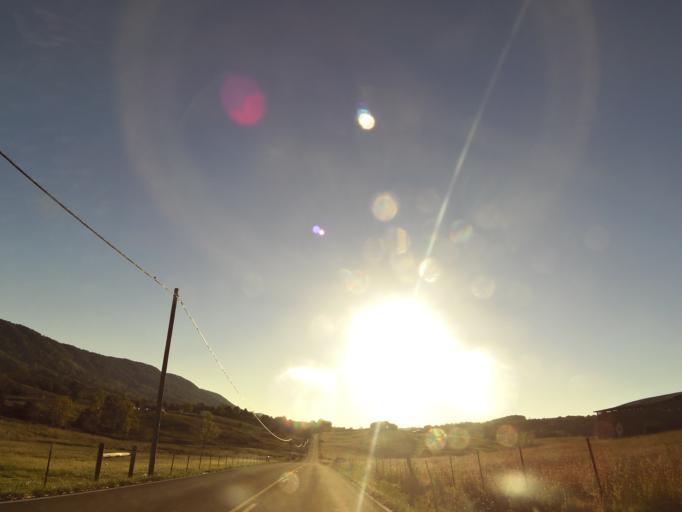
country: US
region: Tennessee
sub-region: Grainger County
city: Rutledge
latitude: 36.3510
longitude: -83.4461
